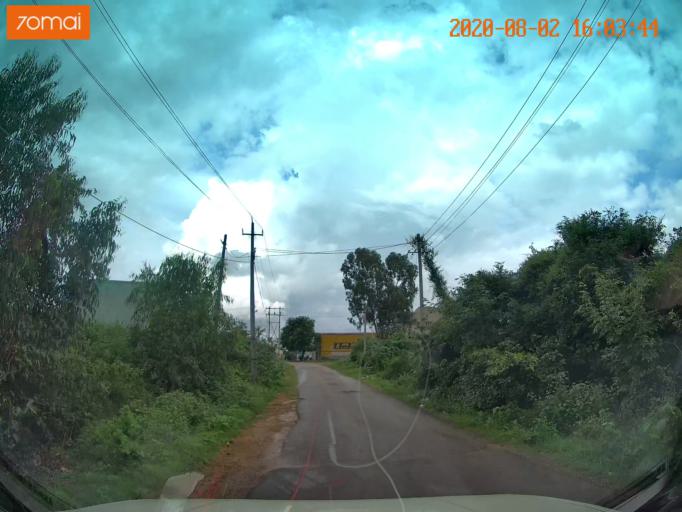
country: IN
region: Karnataka
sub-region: Bangalore Urban
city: Anekal
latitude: 12.8295
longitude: 77.6365
